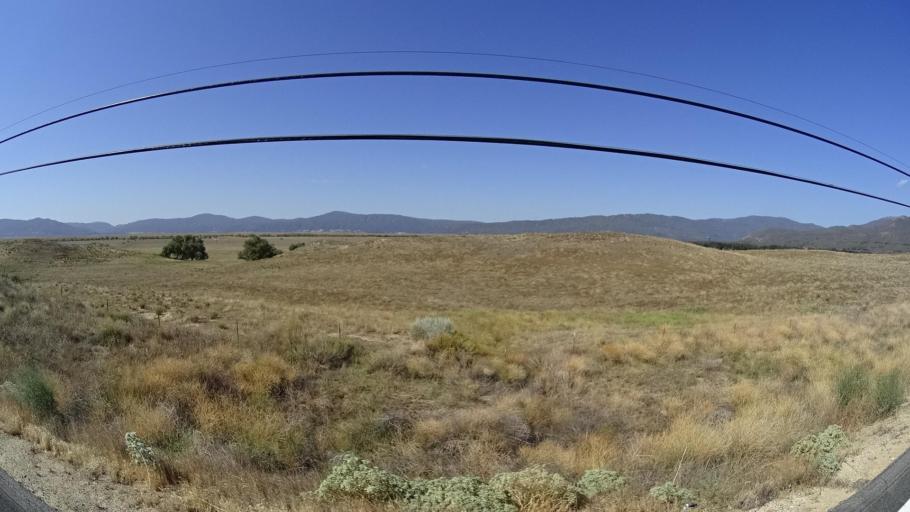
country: US
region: California
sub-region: Riverside County
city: Aguanga
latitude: 33.2950
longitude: -116.6869
